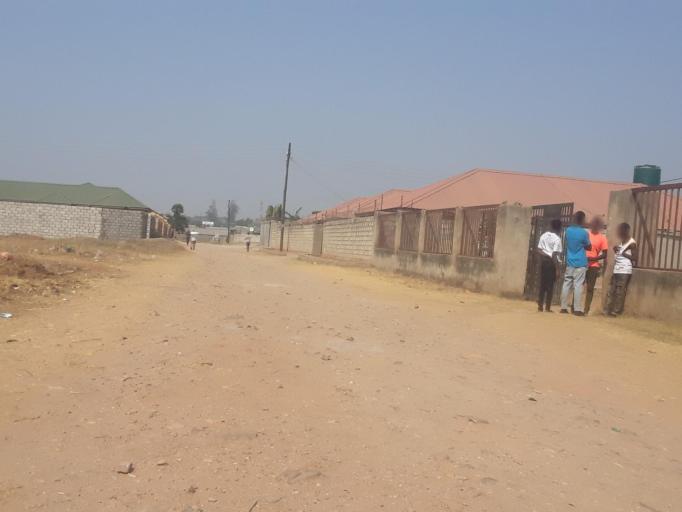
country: ZM
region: Lusaka
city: Lusaka
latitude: -15.3664
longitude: 28.2892
